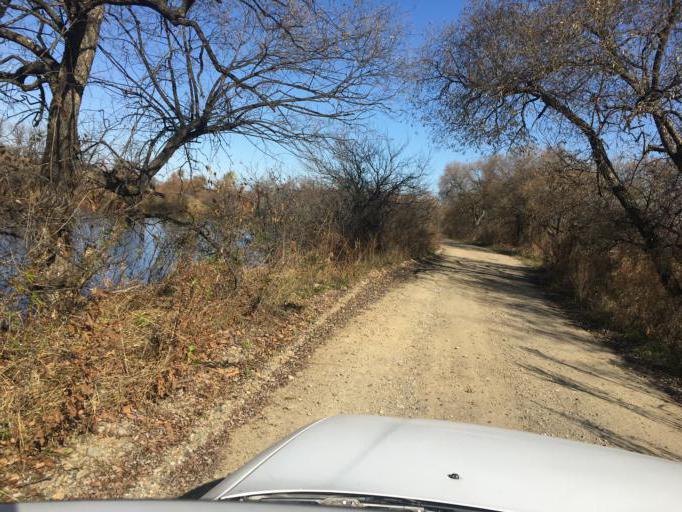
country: RU
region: Primorskiy
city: Dal'nerechensk
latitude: 45.9175
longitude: 133.7882
